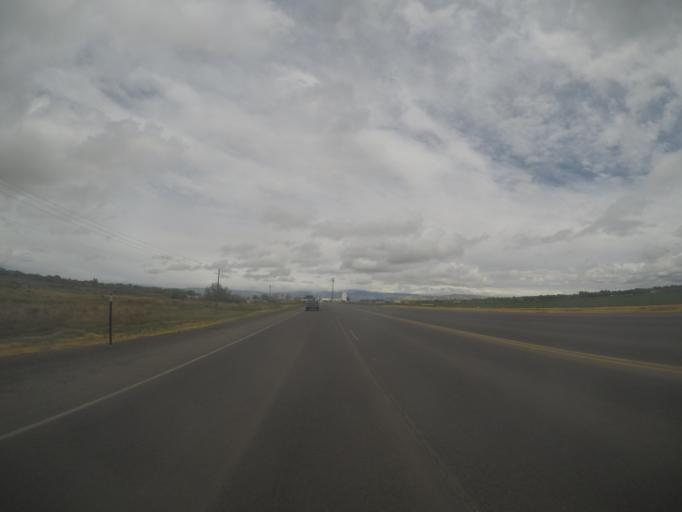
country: US
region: Wyoming
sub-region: Big Horn County
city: Lovell
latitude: 44.8371
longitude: -108.4258
